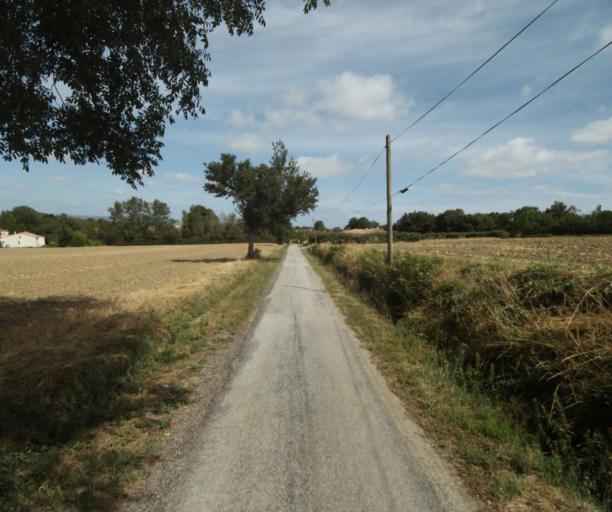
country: FR
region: Midi-Pyrenees
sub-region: Departement du Tarn
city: Soreze
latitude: 43.4637
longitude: 2.1032
